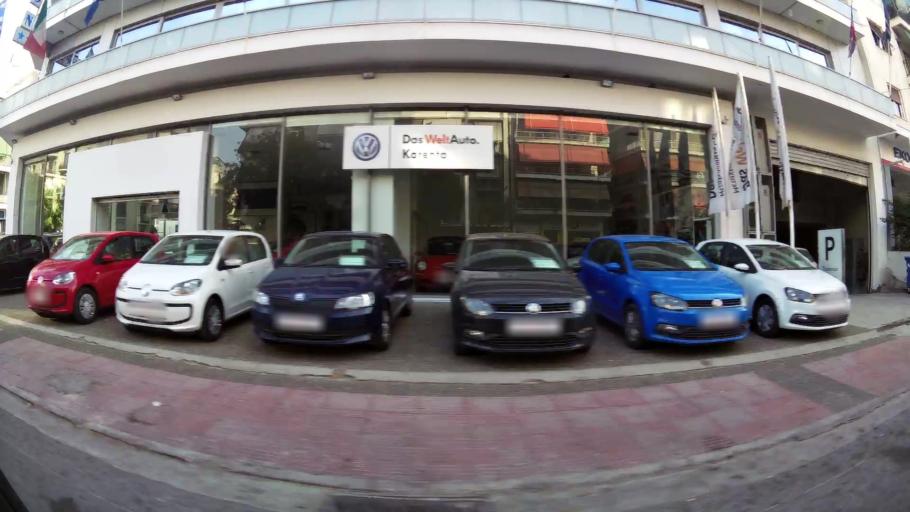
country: GR
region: Attica
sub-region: Nomarchia Athinas
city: Nea Chalkidona
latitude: 38.0152
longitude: 23.7284
